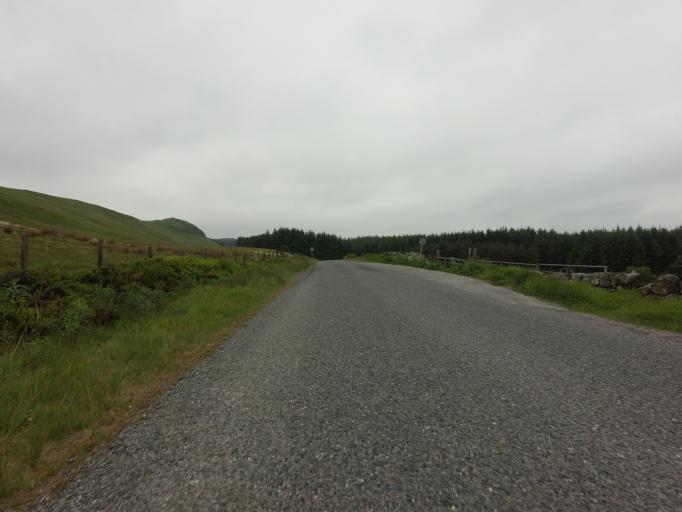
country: GB
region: Scotland
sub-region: Perth and Kinross
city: Kinross
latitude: 56.1570
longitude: -3.4603
